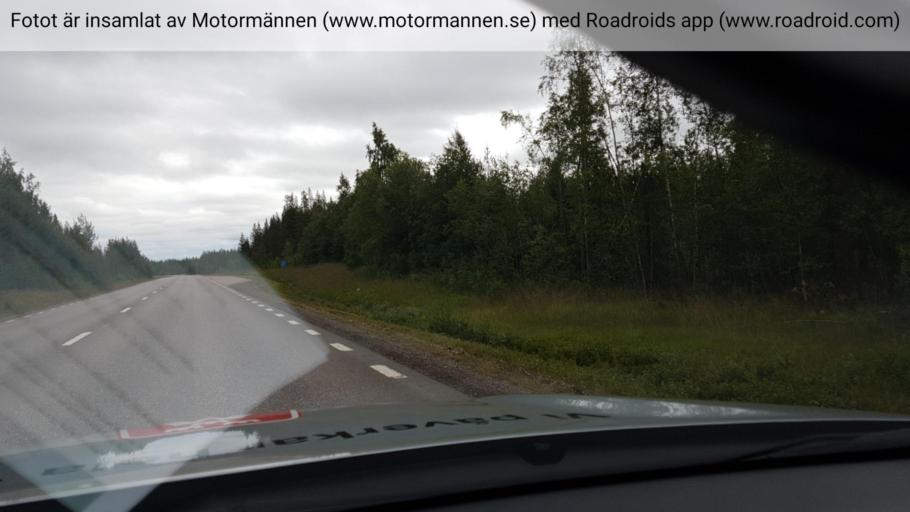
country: SE
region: Norrbotten
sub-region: Gallivare Kommun
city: Gaellivare
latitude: 67.0702
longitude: 21.1132
